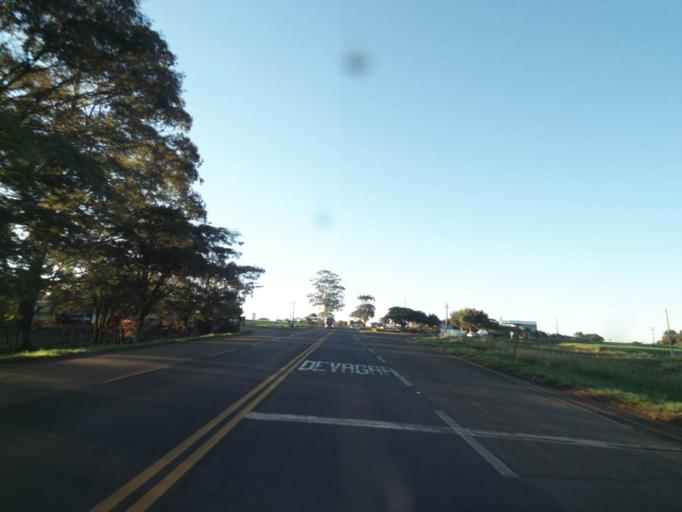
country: BR
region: Parana
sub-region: Faxinal
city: Faxinal
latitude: -23.7014
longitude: -51.1206
